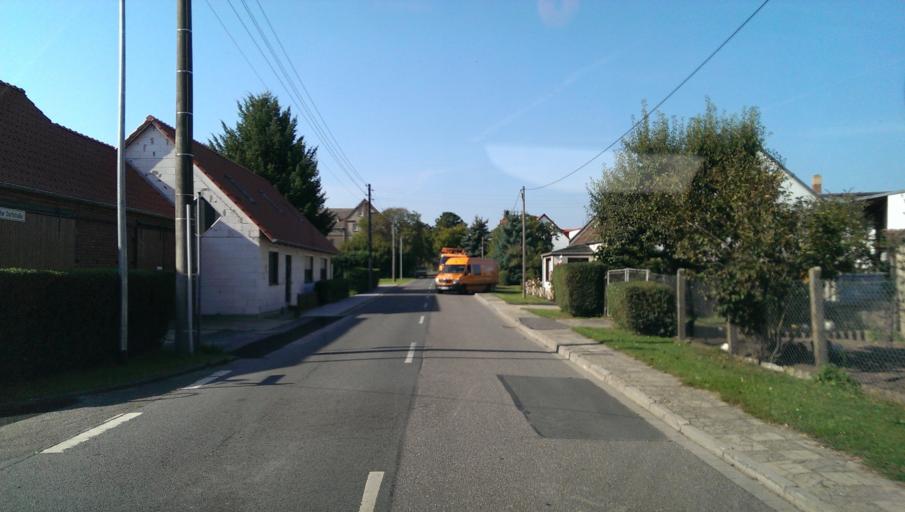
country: DE
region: Saxony-Anhalt
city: Kropstadt
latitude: 51.9894
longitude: 12.6789
